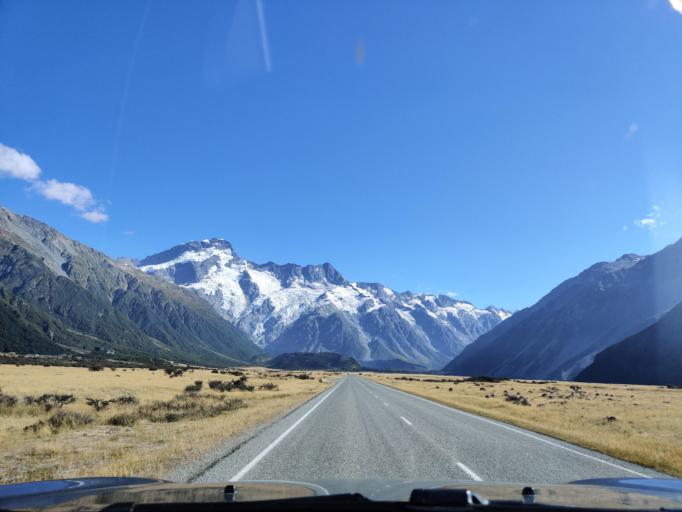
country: NZ
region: Canterbury
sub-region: Timaru District
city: Pleasant Point
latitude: -43.7464
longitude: 170.1148
